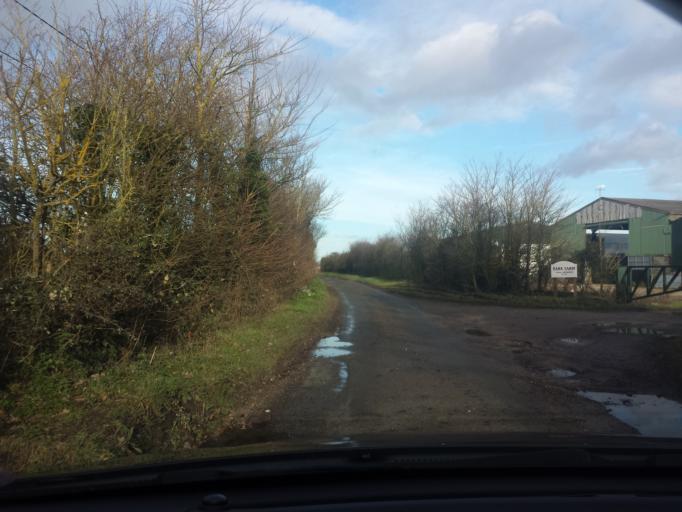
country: GB
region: England
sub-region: Essex
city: Great Bentley
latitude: 51.8926
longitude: 1.0561
